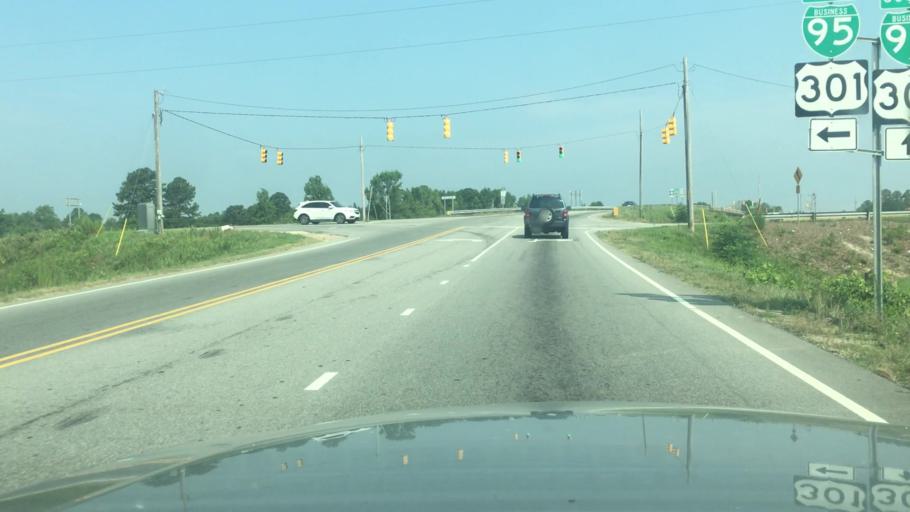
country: US
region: North Carolina
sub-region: Cumberland County
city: Hope Mills
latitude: 34.9436
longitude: -78.9295
